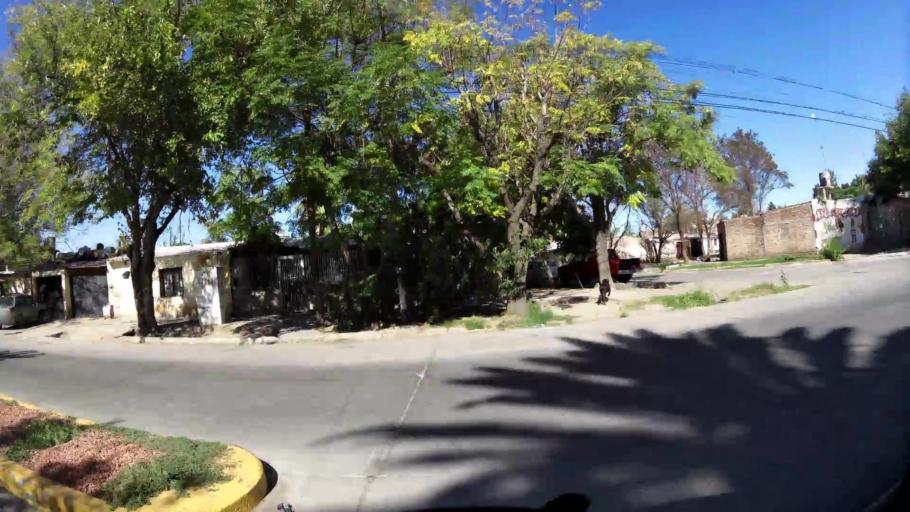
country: AR
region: Mendoza
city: Las Heras
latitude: -32.8408
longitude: -68.8191
